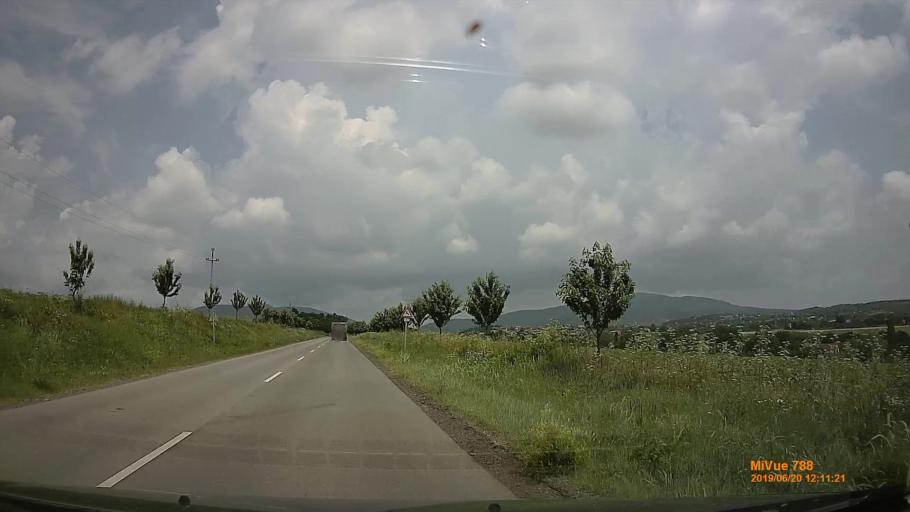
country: HU
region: Baranya
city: Hosszuheteny
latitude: 46.1358
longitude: 18.3480
